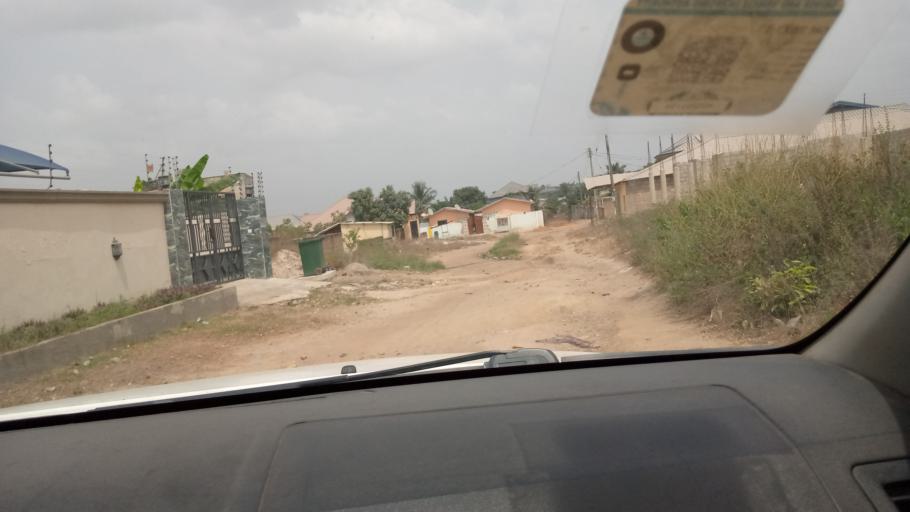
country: GH
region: Central
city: Kasoa
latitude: 5.5348
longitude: -0.4502
